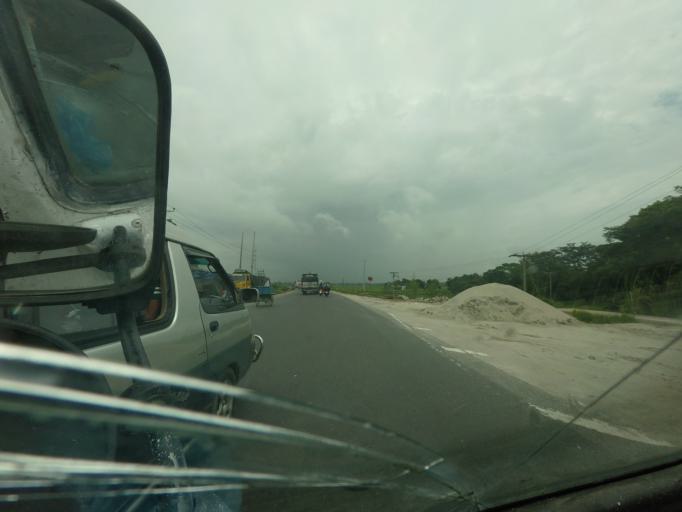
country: BD
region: Dhaka
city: Char Bhadrasan
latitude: 23.3708
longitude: 90.0352
